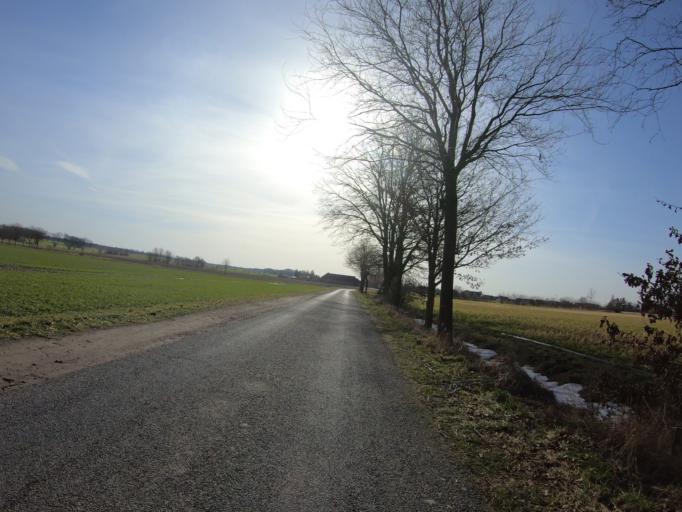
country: DE
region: Lower Saxony
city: Isenbuttel
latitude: 52.4135
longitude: 10.5646
